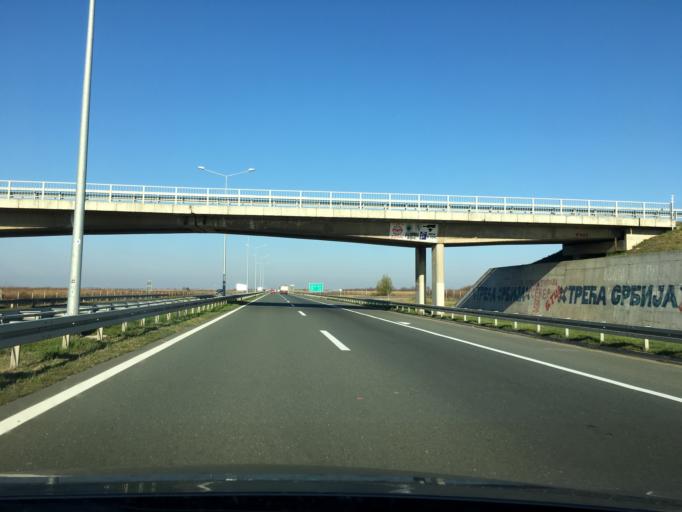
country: RS
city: Rumenka
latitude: 45.3171
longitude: 19.7946
